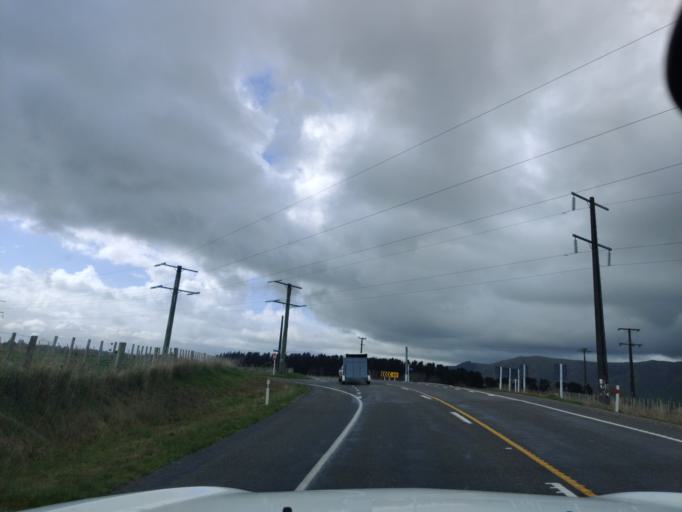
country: NZ
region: Manawatu-Wanganui
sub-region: Palmerston North City
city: Palmerston North
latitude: -40.4468
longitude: 175.5427
